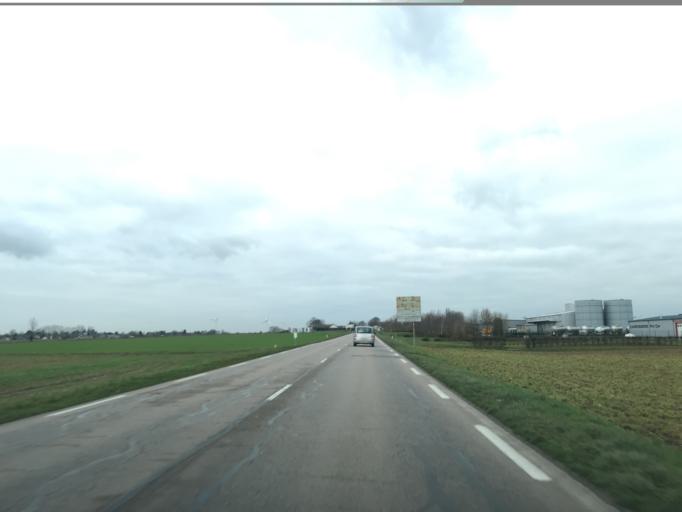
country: FR
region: Haute-Normandie
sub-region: Departement de l'Eure
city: Fleury-sur-Andelle
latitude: 49.3803
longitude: 1.3210
